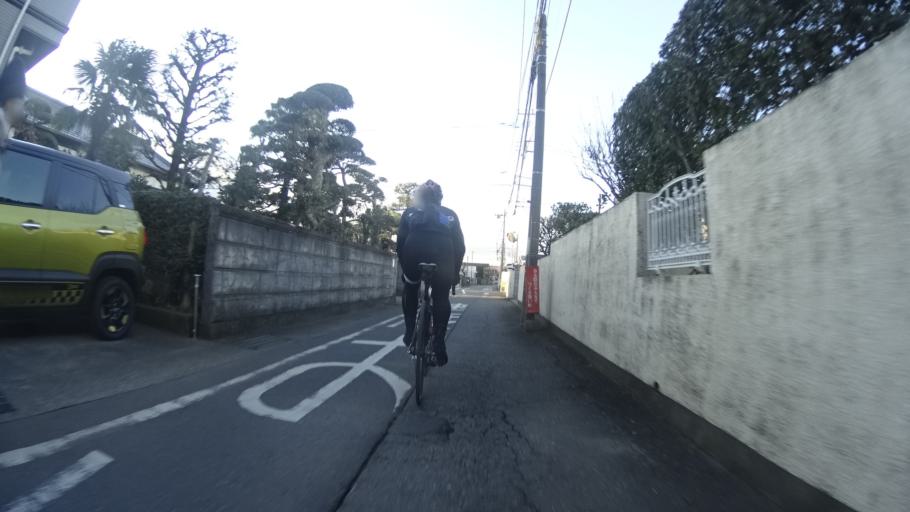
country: JP
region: Kanagawa
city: Atsugi
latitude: 35.4638
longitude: 139.3691
